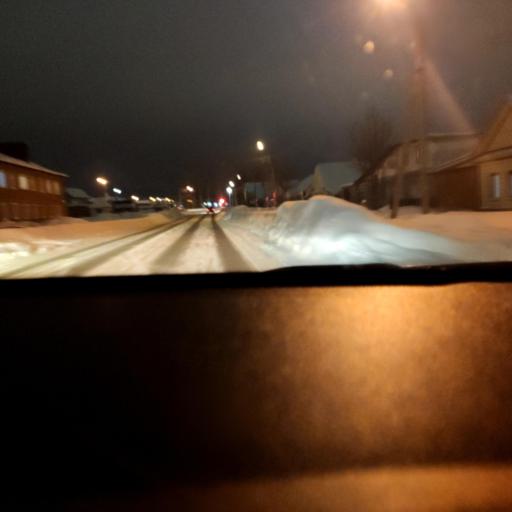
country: RU
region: Tatarstan
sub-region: Chistopol'skiy Rayon
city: Chistopol'
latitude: 55.3562
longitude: 50.6612
